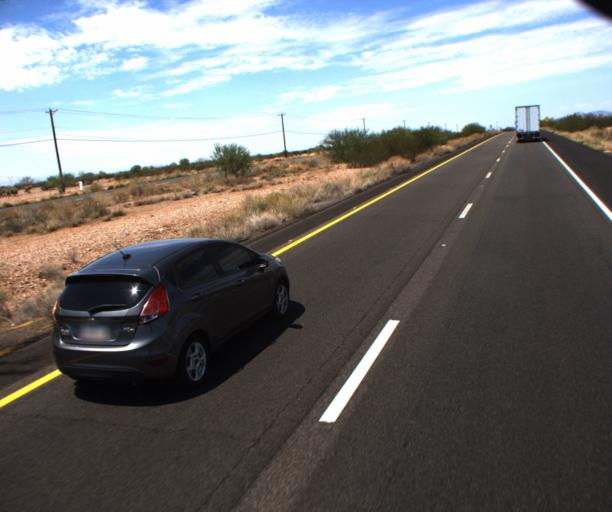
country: US
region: Arizona
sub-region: Pinal County
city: Gold Camp
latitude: 33.2793
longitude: -111.3675
